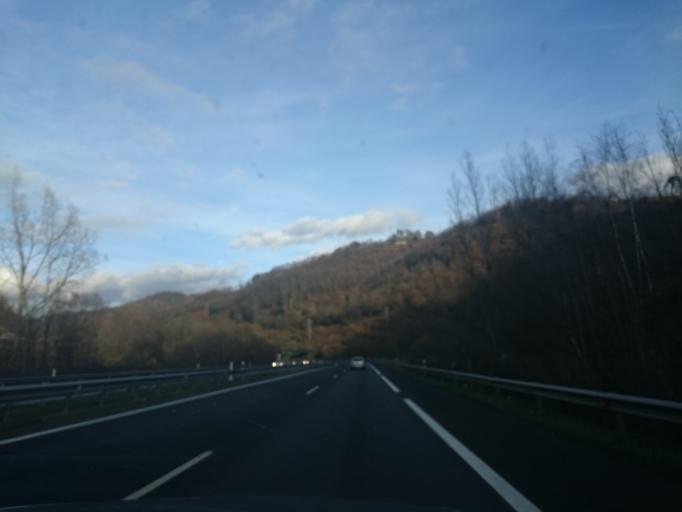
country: ES
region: Asturias
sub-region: Province of Asturias
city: Pola de Lena
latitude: 43.1870
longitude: -5.7960
